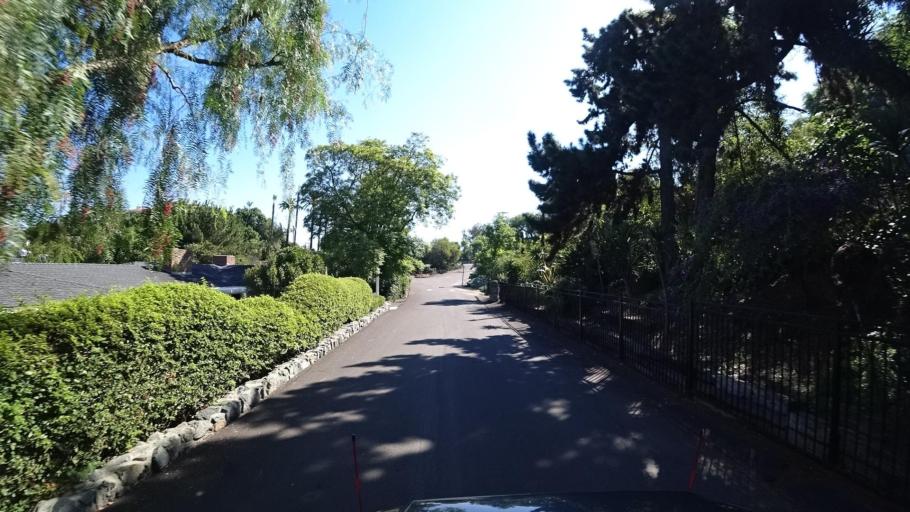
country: US
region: California
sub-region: San Diego County
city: Casa de Oro-Mount Helix
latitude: 32.7691
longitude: -116.9829
